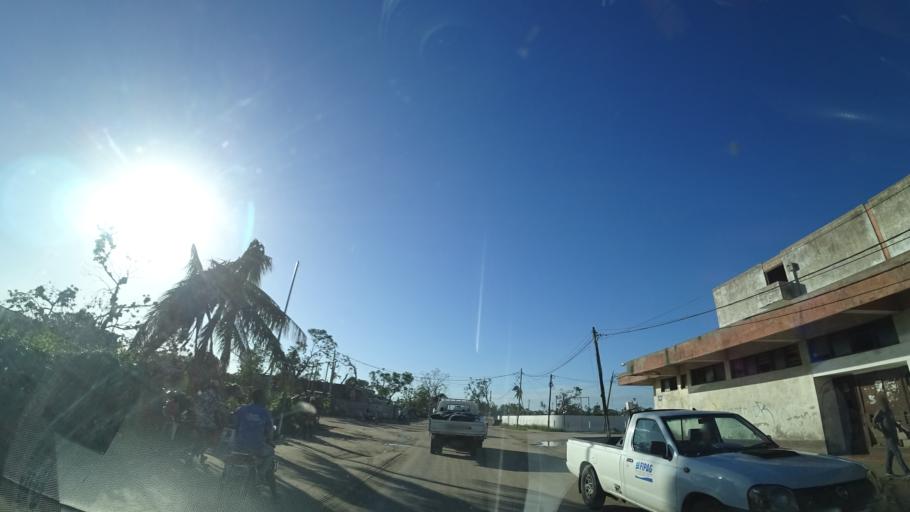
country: MZ
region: Sofala
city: Beira
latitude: -19.7787
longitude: 34.8720
